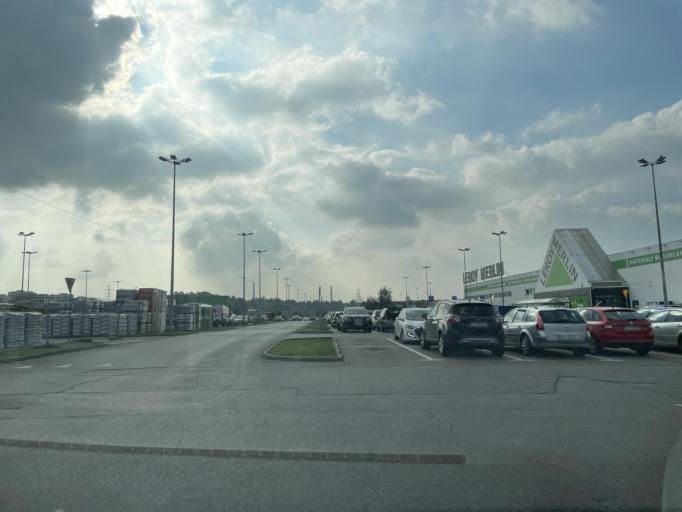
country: PL
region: Silesian Voivodeship
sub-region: Powiat bedzinski
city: Bedzin
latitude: 50.3016
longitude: 19.1668
